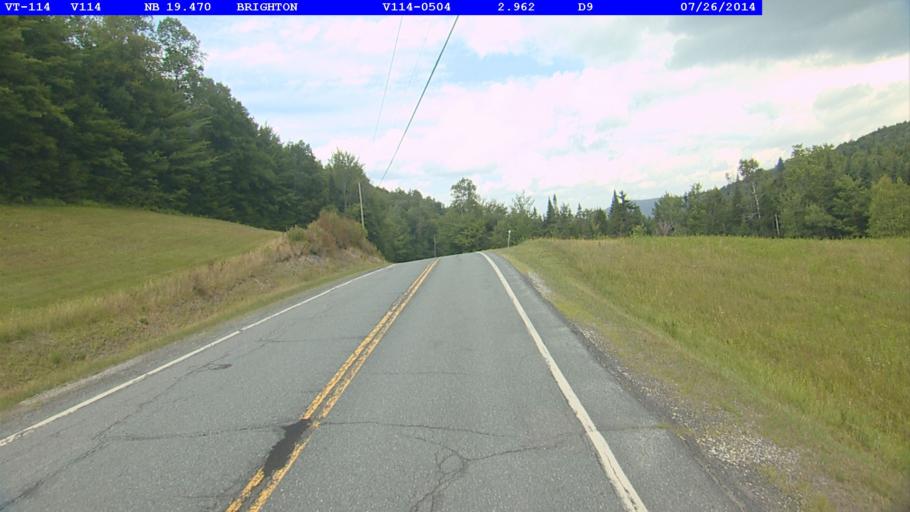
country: US
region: Vermont
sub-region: Caledonia County
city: Lyndonville
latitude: 44.7770
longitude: -71.9078
